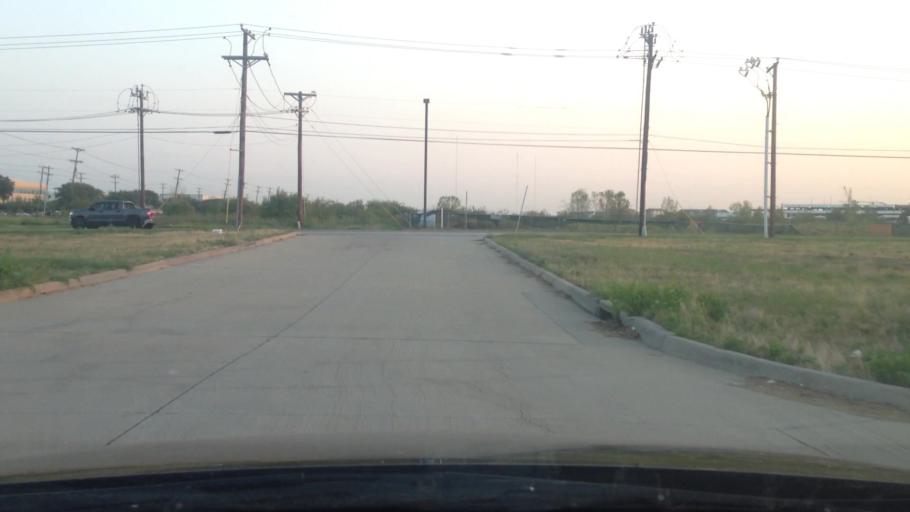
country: US
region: Texas
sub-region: Dallas County
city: Coppell
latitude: 32.9251
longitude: -96.9927
